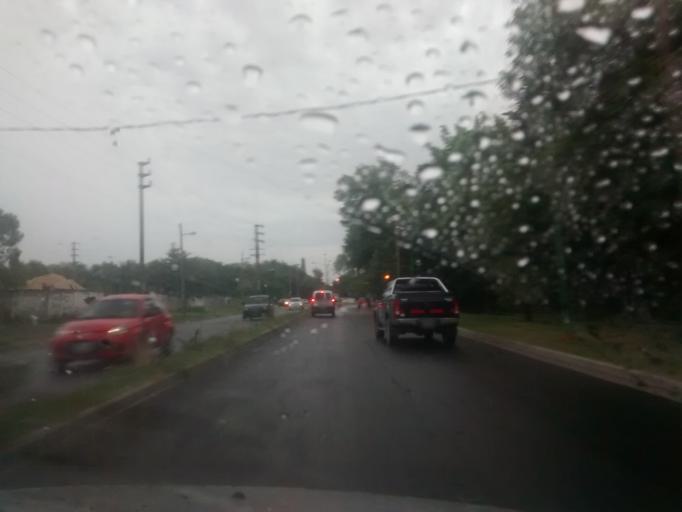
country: AR
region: Buenos Aires
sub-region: Partido de La Plata
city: La Plata
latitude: -34.9137
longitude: -58.0060
